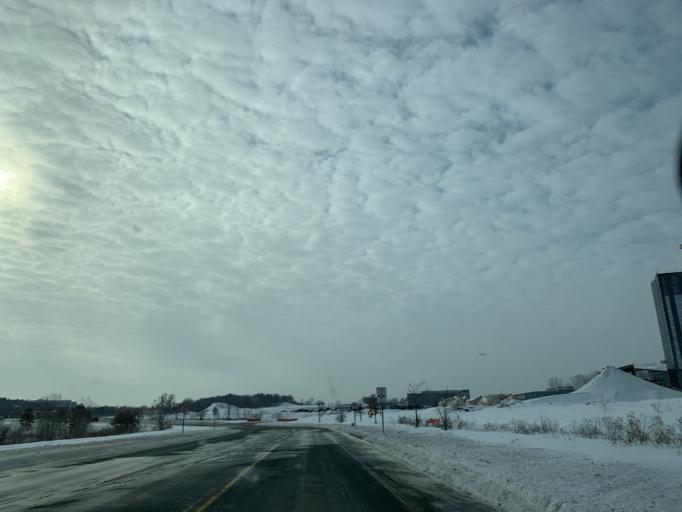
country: US
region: Minnesota
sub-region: Dakota County
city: Mendota Heights
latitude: 44.8605
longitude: -93.1091
